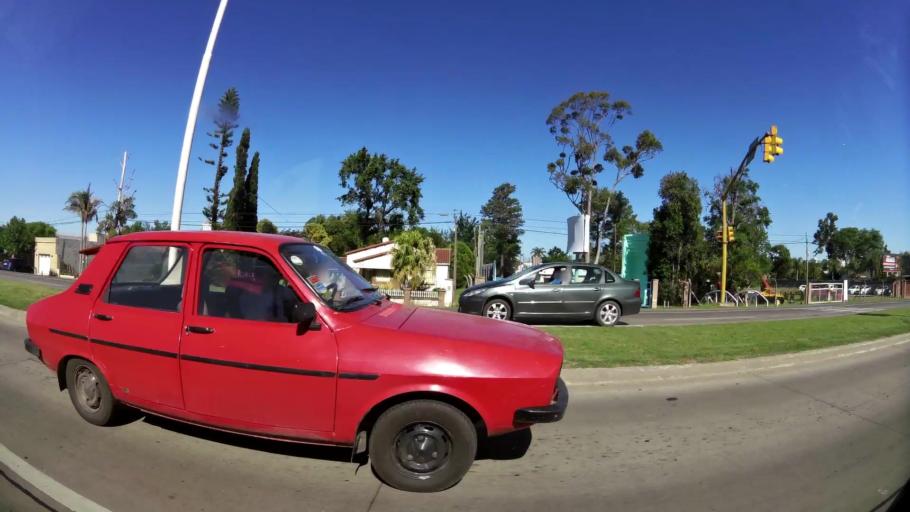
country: AR
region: Santa Fe
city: Rafaela
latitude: -31.2574
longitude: -61.5063
